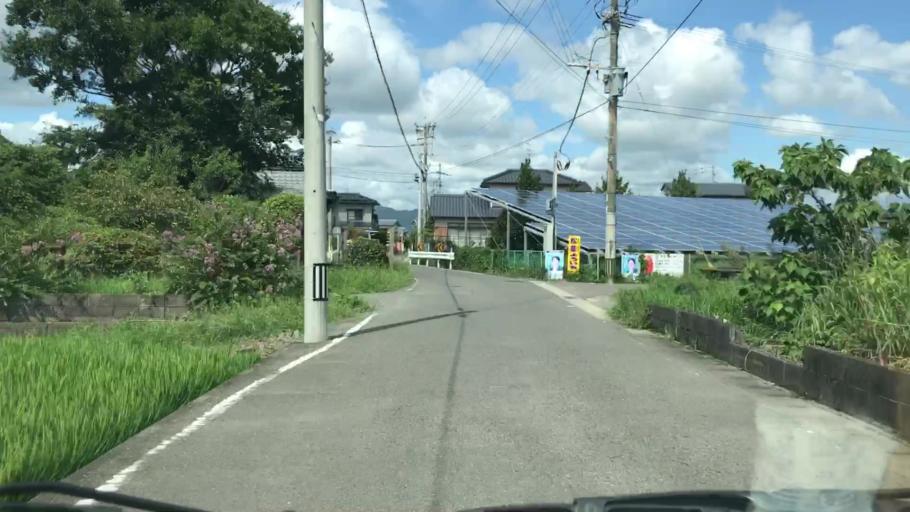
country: JP
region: Saga Prefecture
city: Saga-shi
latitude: 33.2409
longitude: 130.2014
